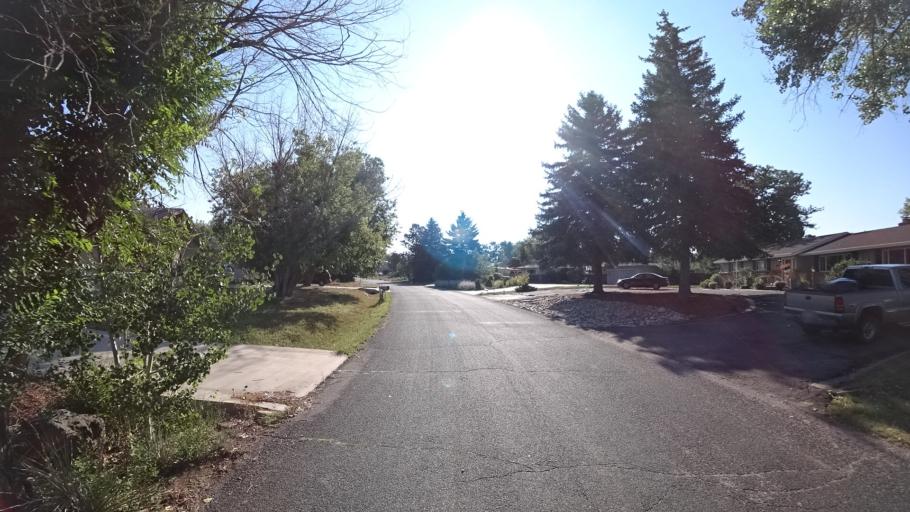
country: US
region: Colorado
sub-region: El Paso County
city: Air Force Academy
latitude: 38.9311
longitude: -104.7898
